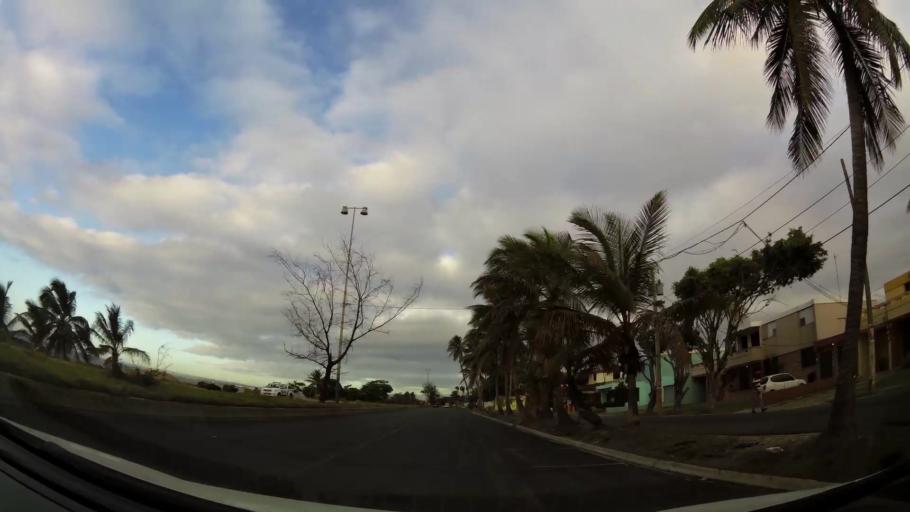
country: DO
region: Nacional
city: Bella Vista
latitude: 18.4269
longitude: -69.9748
